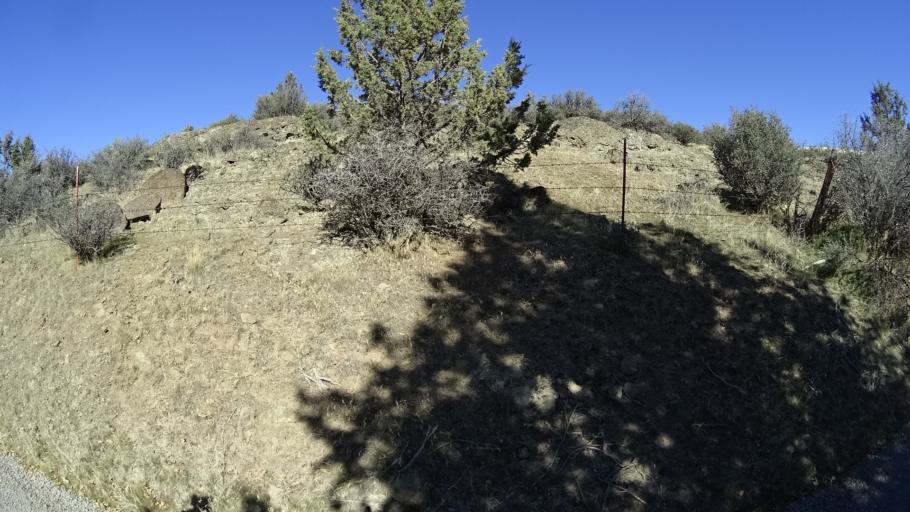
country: US
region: California
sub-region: Siskiyou County
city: Montague
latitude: 41.7931
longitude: -122.3591
